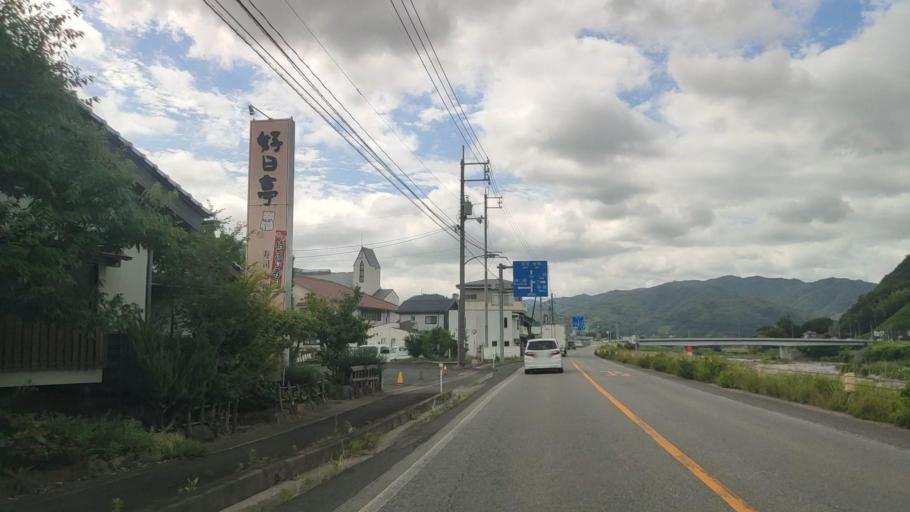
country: JP
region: Tottori
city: Yonago
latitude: 35.3453
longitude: 133.4343
